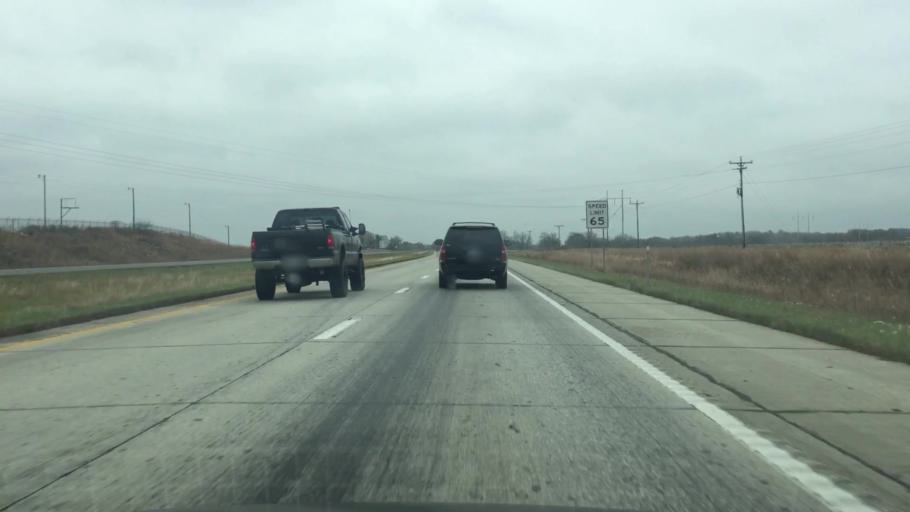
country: US
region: Missouri
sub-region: Saint Clair County
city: Osceola
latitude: 38.0332
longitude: -93.6778
